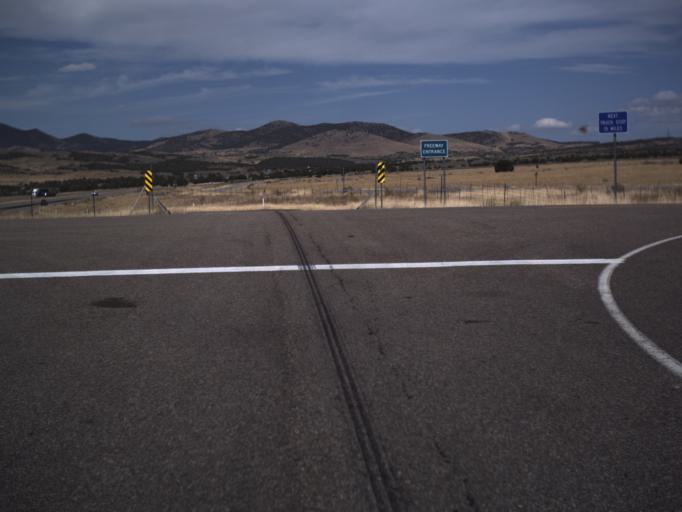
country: US
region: Utah
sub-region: Millard County
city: Fillmore
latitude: 39.1437
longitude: -112.2352
